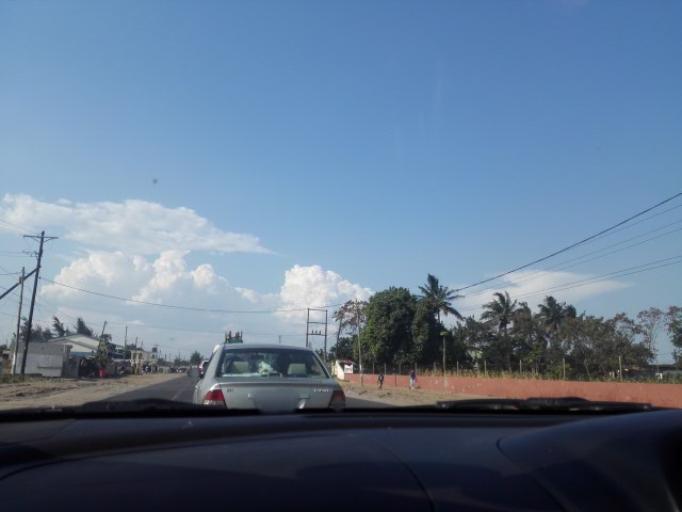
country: MZ
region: Maputo City
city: Maputo
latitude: -25.8582
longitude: 32.5669
